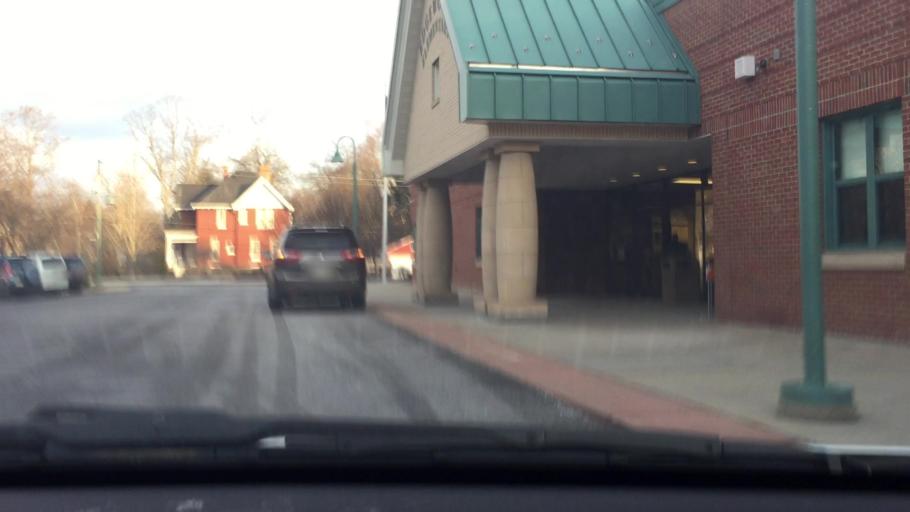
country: US
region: Pennsylvania
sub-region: Allegheny County
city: Edgeworth
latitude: 40.5485
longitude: -80.1913
